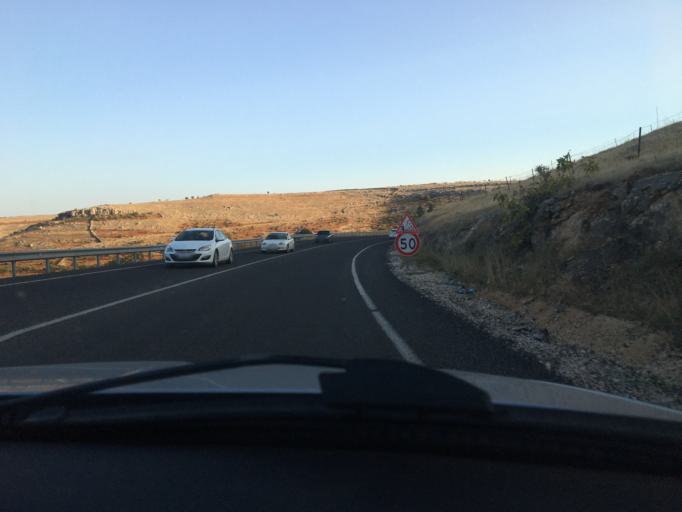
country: TR
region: Sanliurfa
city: Halfeti
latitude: 37.2261
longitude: 37.9585
